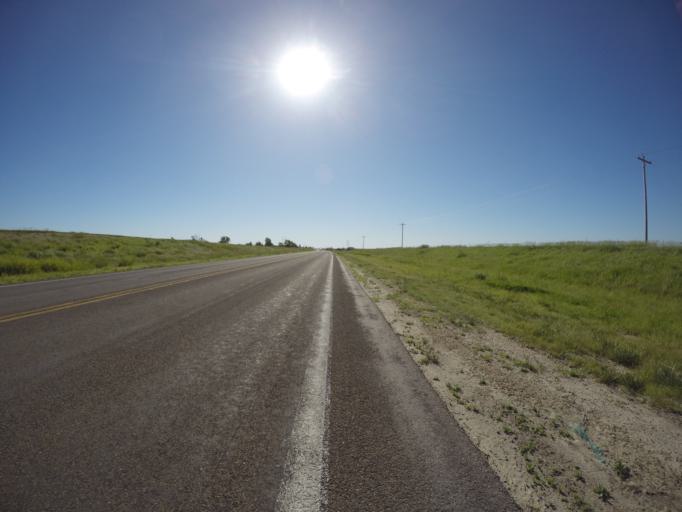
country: US
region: Kansas
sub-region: Norton County
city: Norton
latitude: 39.8277
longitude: -100.0082
